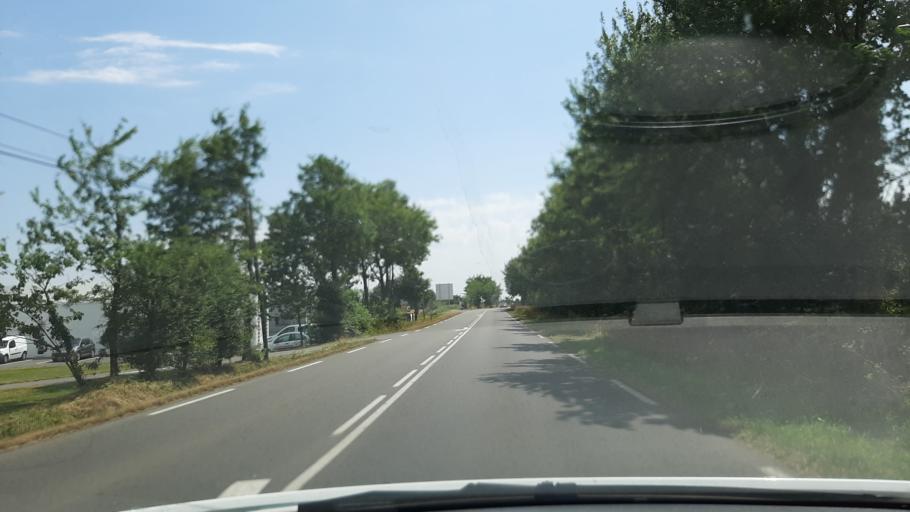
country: FR
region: Pays de la Loire
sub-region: Departement de la Vendee
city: Le Poire-sur-Vie
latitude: 46.7627
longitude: -1.4894
